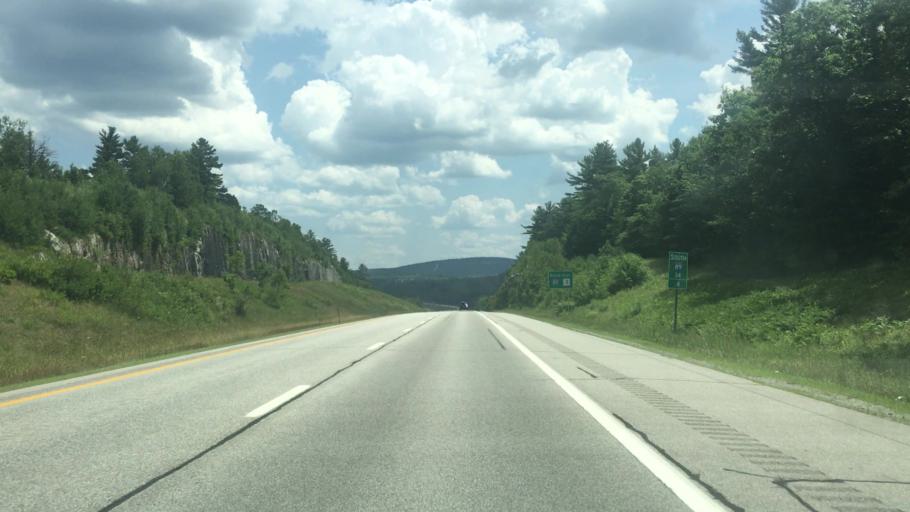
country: US
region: New Hampshire
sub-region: Merrimack County
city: New London
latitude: 43.4162
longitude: -72.0324
